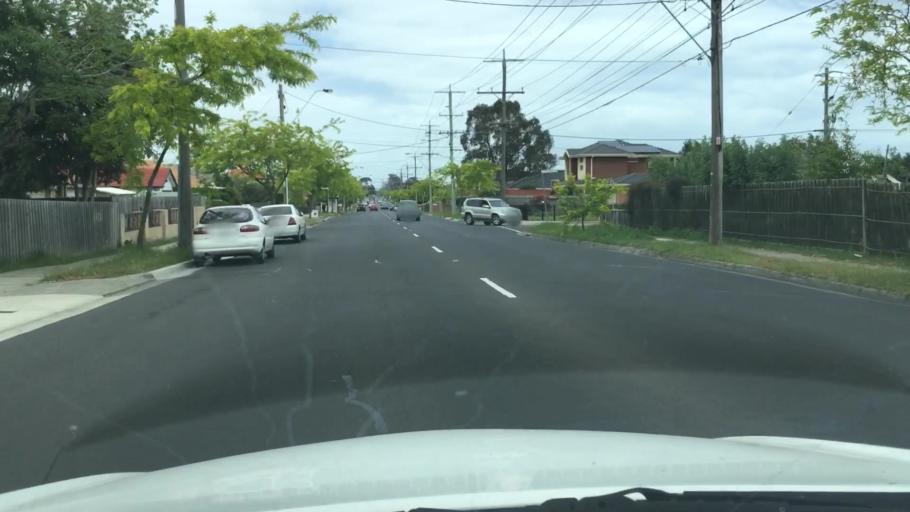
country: AU
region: Victoria
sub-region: Greater Dandenong
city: Noble Park
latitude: -37.9745
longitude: 145.1665
